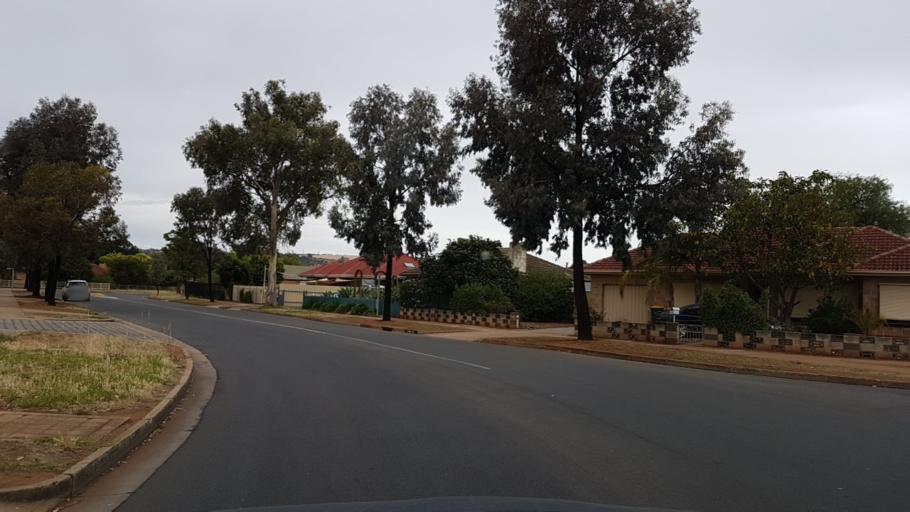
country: AU
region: South Australia
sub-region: Salisbury
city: Elizabeth
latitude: -34.7337
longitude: 138.6623
